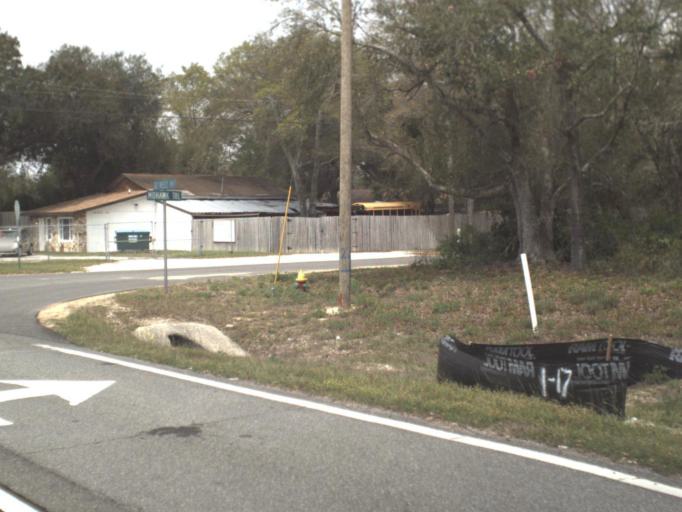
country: US
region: Florida
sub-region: Santa Rosa County
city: Woodlawn Beach
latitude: 30.3965
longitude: -87.0226
